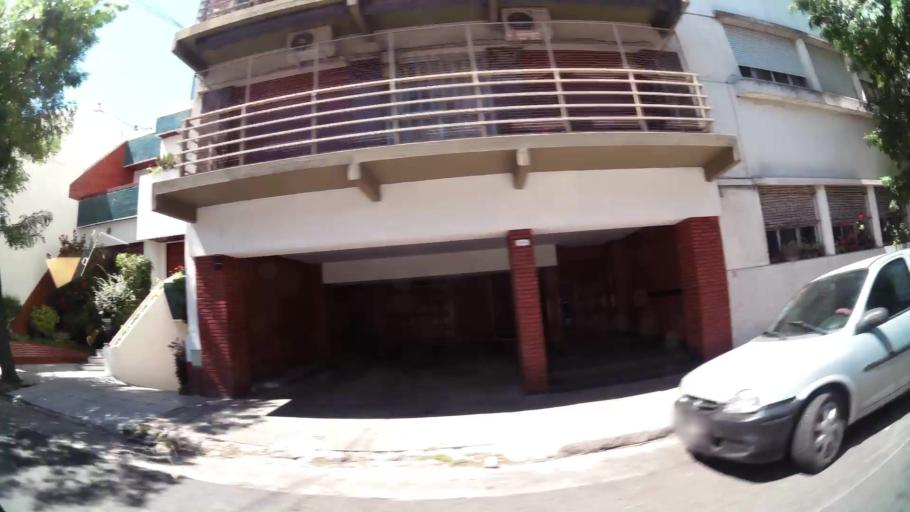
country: AR
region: Buenos Aires F.D.
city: Buenos Aires
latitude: -34.6285
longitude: -58.4090
